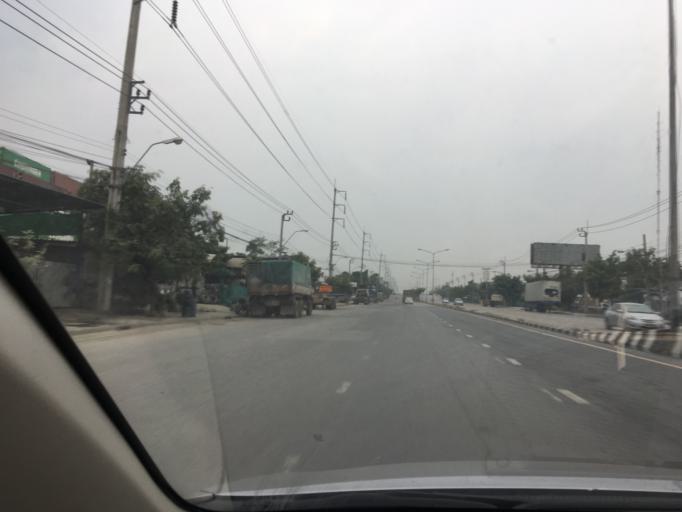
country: TH
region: Bangkok
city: Lat Krabang
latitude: 13.7547
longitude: 100.7580
